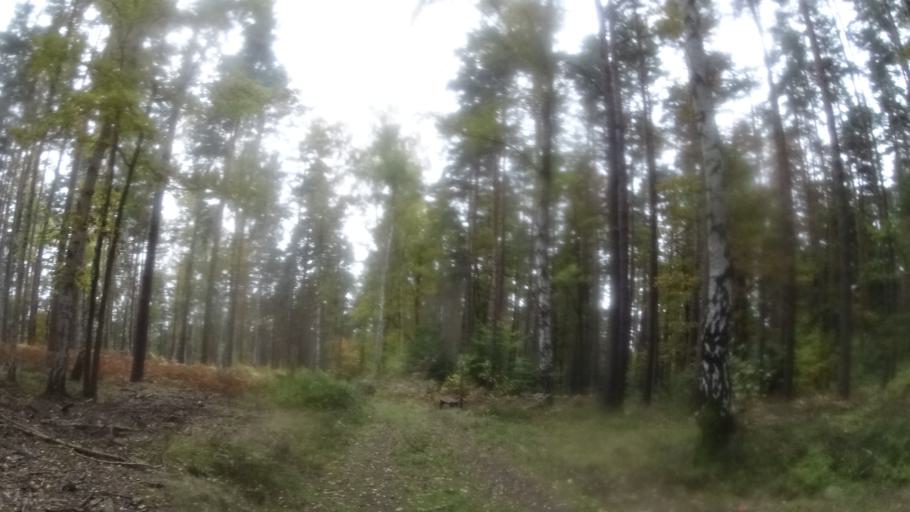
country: DE
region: Thuringia
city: Grosseutersdorf
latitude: 50.7760
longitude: 11.5655
